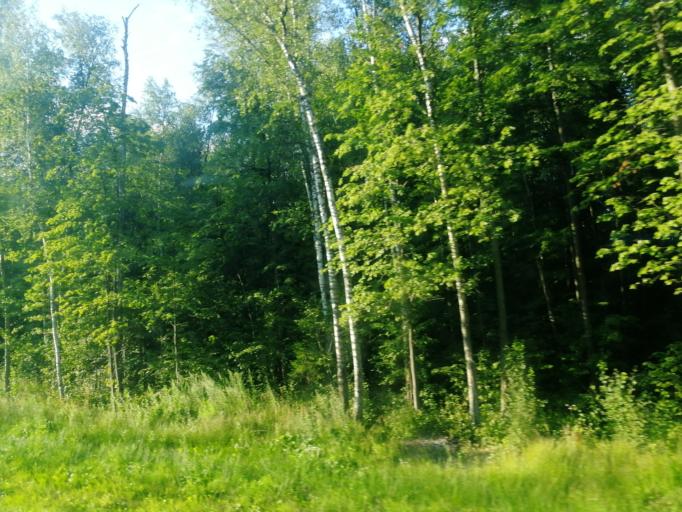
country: RU
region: Kaluga
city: Kaluga
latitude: 54.4470
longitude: 36.3115
